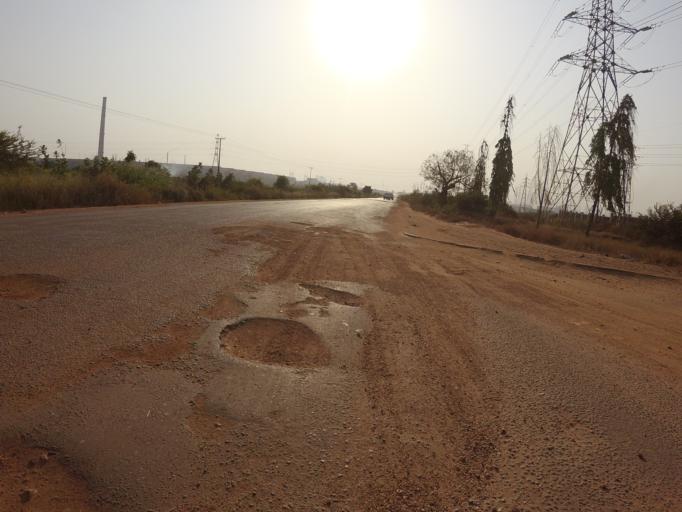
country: GH
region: Greater Accra
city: Tema
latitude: 5.6735
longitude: 0.0260
